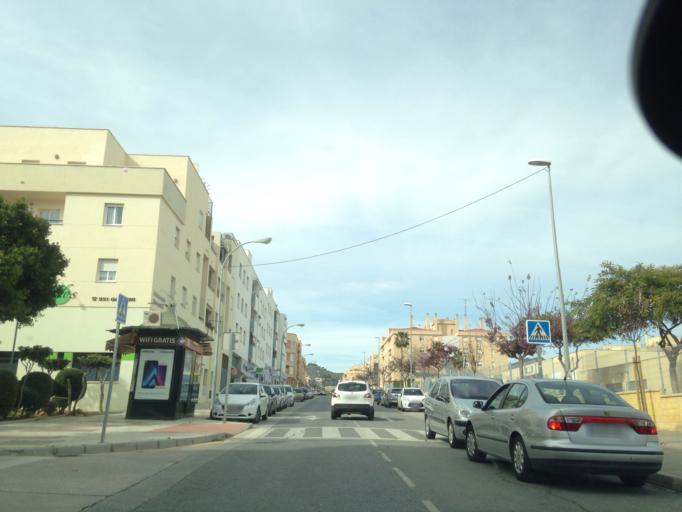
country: ES
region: Andalusia
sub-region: Provincia de Malaga
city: Malaga
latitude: 36.7223
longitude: -4.4648
